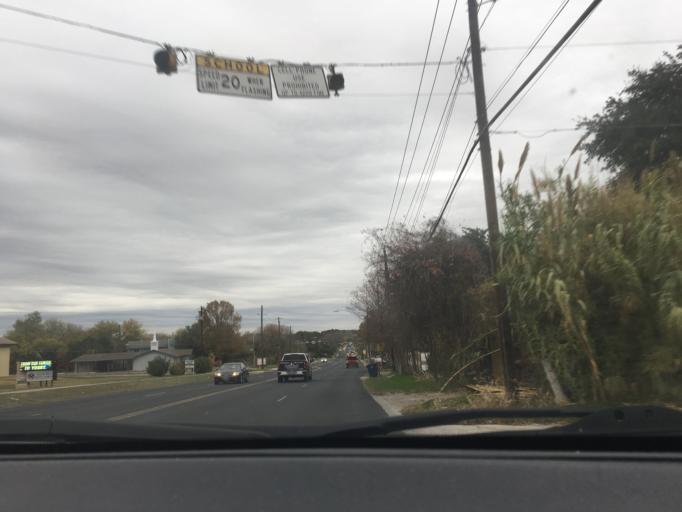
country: US
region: Texas
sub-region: Travis County
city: Onion Creek
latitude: 30.1798
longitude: -97.7958
